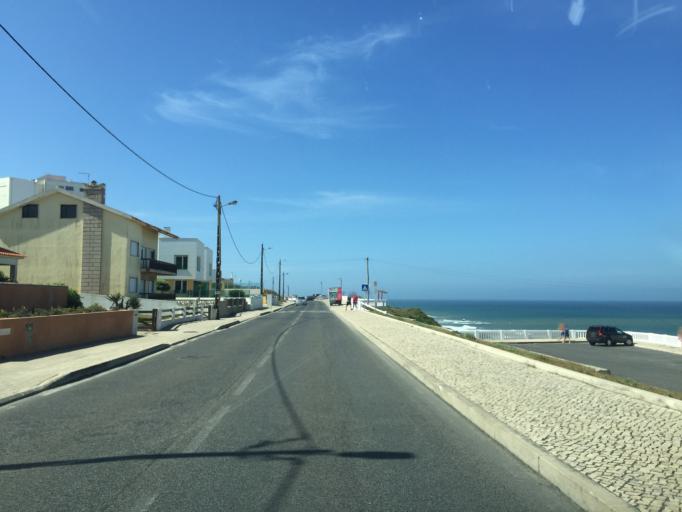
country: PT
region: Lisbon
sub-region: Torres Vedras
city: Silveira
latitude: 39.1419
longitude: -9.3758
